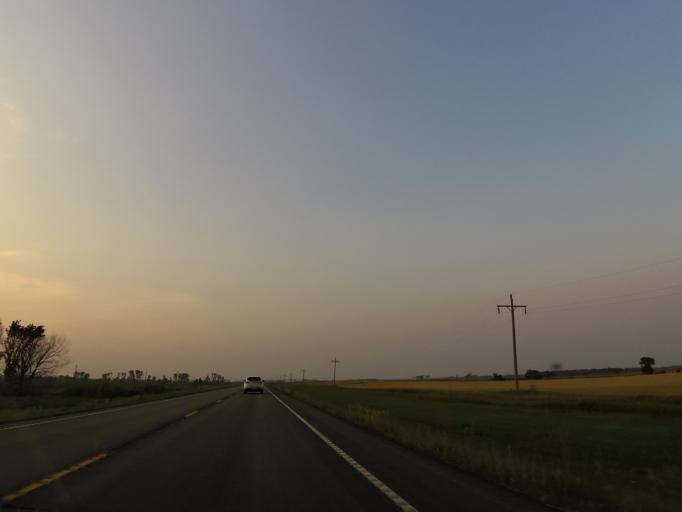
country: US
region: North Dakota
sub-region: Walsh County
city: Park River
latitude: 48.1863
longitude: -97.6218
